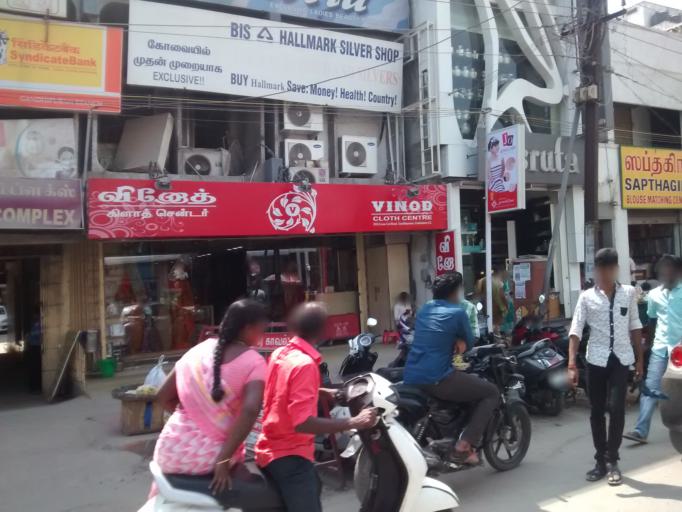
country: IN
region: Tamil Nadu
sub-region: Coimbatore
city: Coimbatore
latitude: 11.0170
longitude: 76.9654
